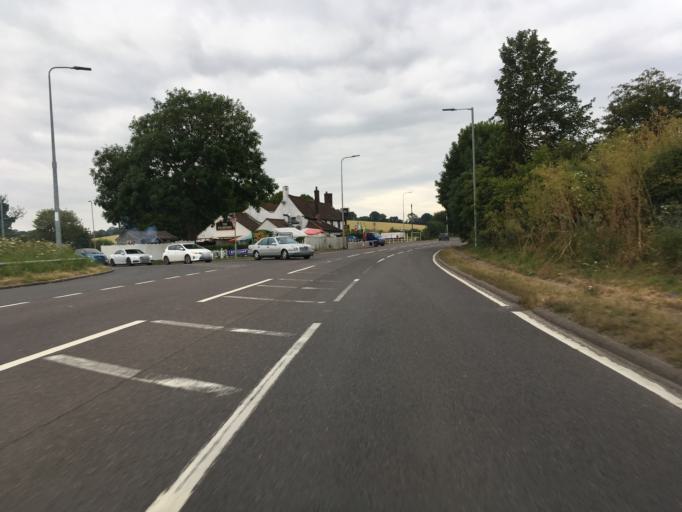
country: GB
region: England
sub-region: Hertfordshire
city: Markyate
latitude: 51.8497
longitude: -0.4765
